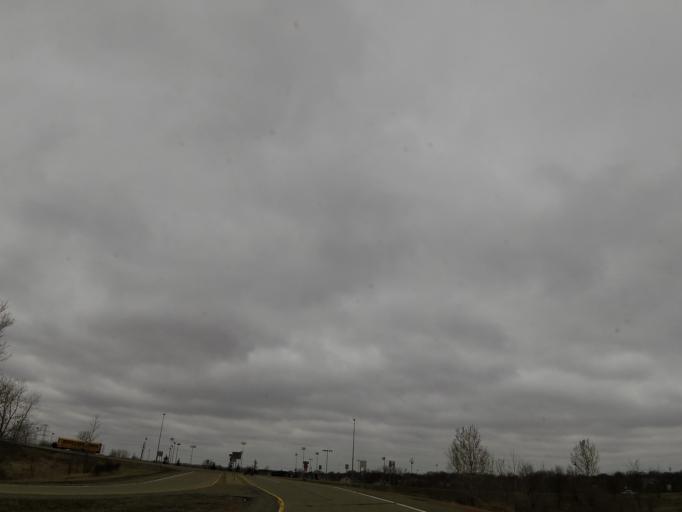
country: US
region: Minnesota
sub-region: Scott County
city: Shakopee
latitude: 44.7774
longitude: -93.5388
